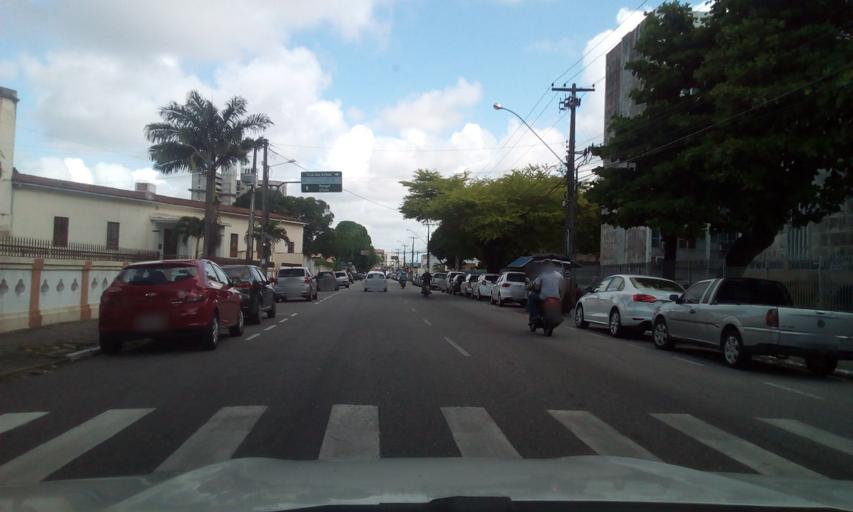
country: BR
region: Paraiba
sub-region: Joao Pessoa
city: Joao Pessoa
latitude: -7.1331
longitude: -34.8801
